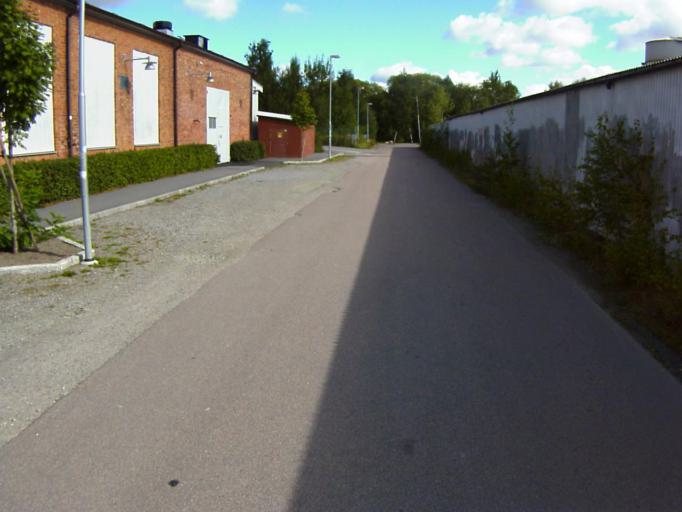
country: SE
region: Soedermanland
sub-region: Eskilstuna Kommun
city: Eskilstuna
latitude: 59.3759
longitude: 16.5011
